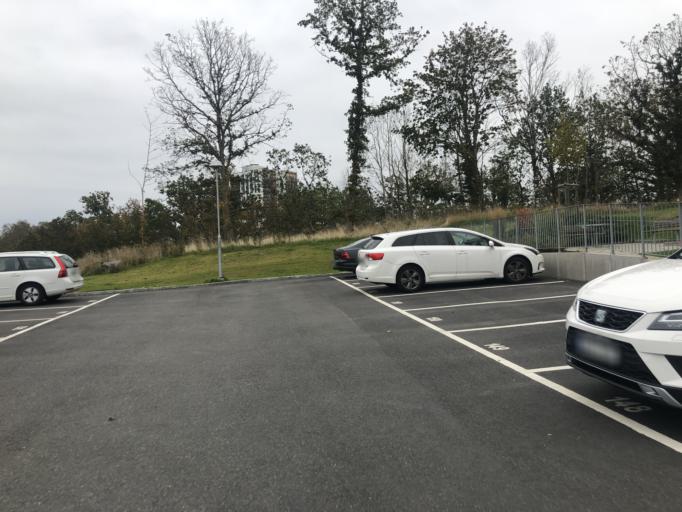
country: SE
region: Vaestra Goetaland
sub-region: Molndal
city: Moelndal
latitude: 57.6587
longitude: 12.0257
